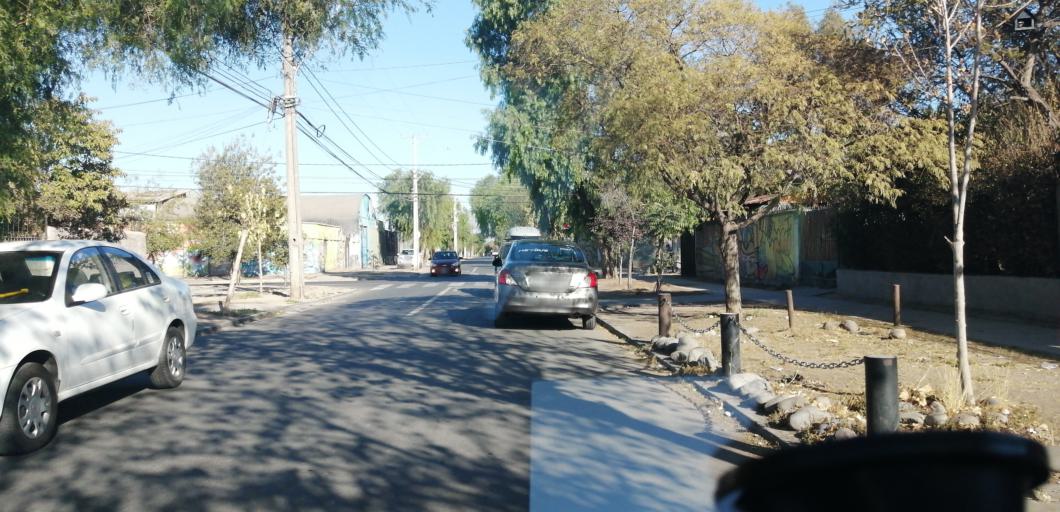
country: CL
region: Santiago Metropolitan
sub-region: Provincia de Santiago
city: Lo Prado
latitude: -33.4384
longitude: -70.7595
